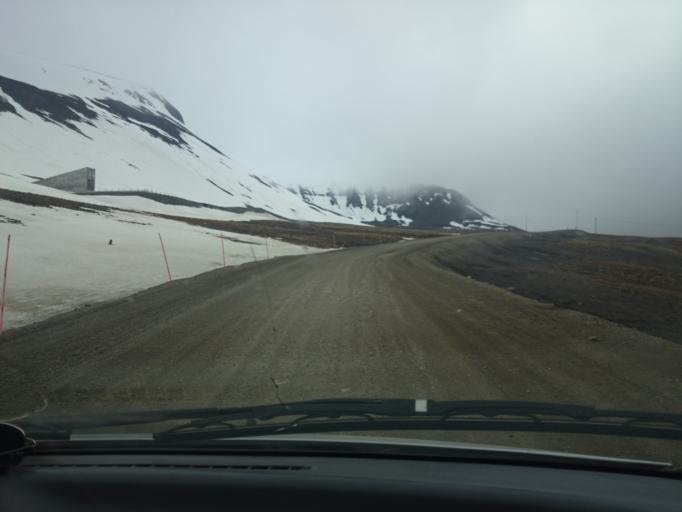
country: SJ
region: Svalbard
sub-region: Spitsbergen
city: Longyearbyen
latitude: 78.2366
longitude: 15.4961
